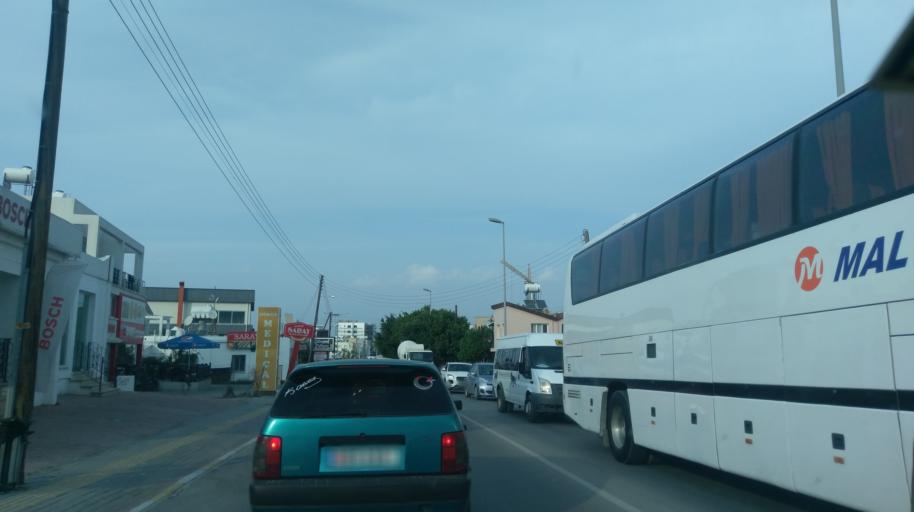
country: CY
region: Keryneia
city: Kyrenia
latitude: 35.3326
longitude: 33.3308
